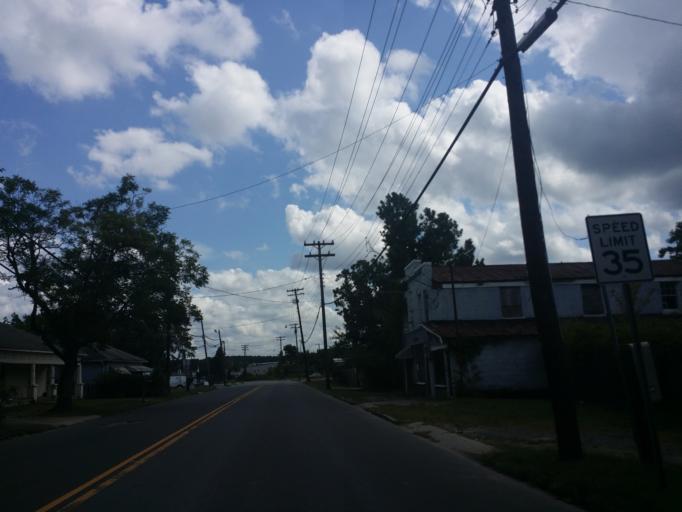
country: US
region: North Carolina
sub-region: Durham County
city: Durham
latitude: 35.9754
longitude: -78.8686
